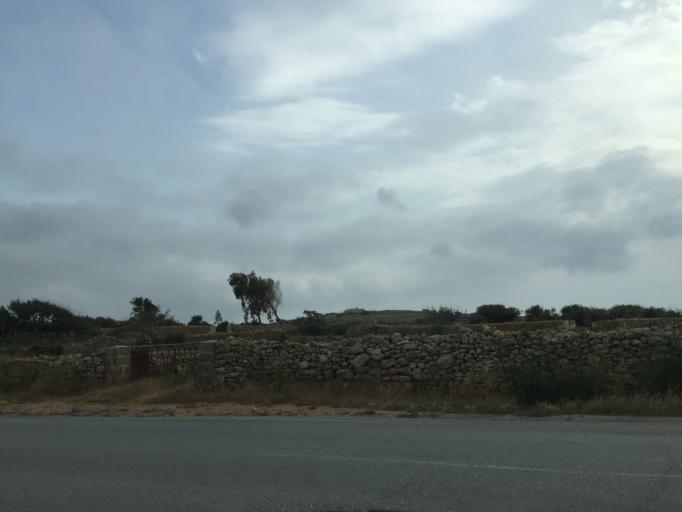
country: MT
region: Il-Mellieha
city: Mellieha
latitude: 35.9461
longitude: 14.3528
